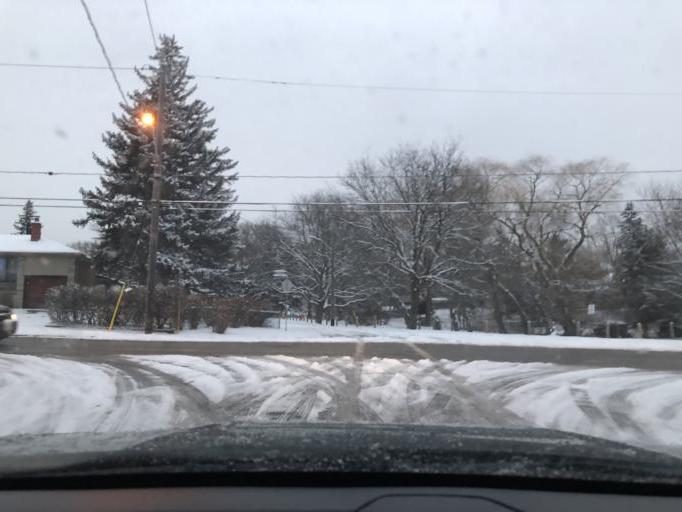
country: CA
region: Ontario
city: Toronto
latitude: 43.6989
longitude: -79.4843
